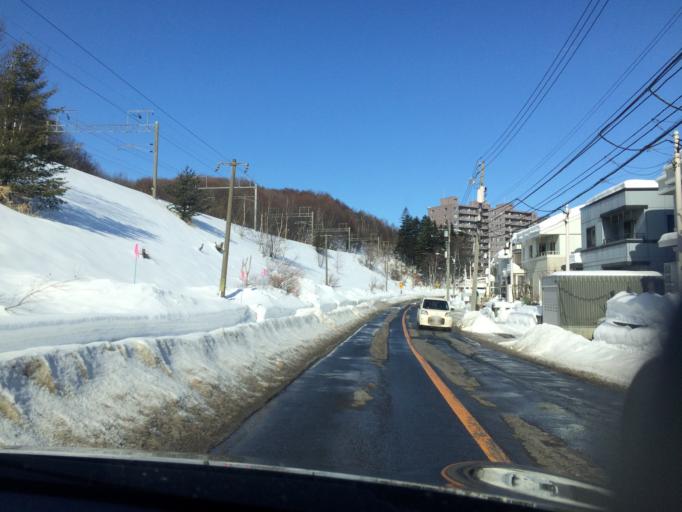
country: JP
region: Hokkaido
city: Kitahiroshima
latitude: 43.0194
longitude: 141.4850
